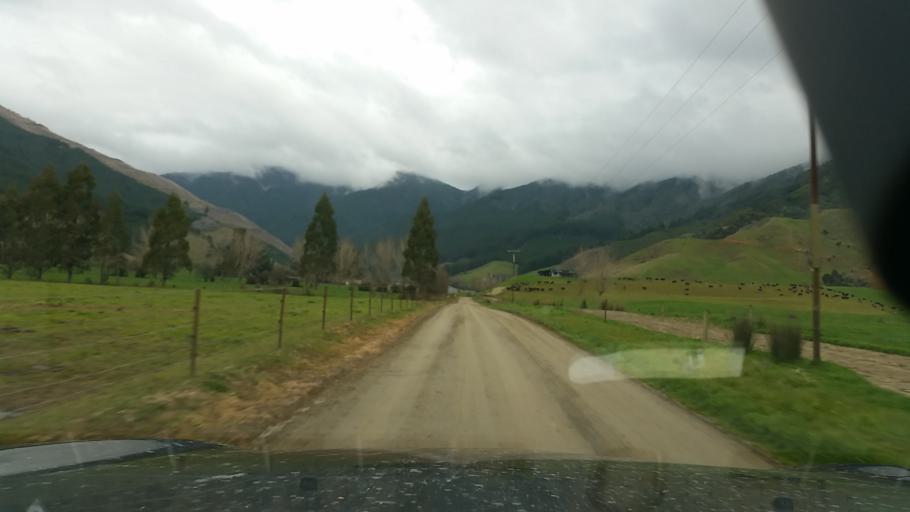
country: NZ
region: Marlborough
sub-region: Marlborough District
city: Picton
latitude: -41.2969
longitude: 173.8556
